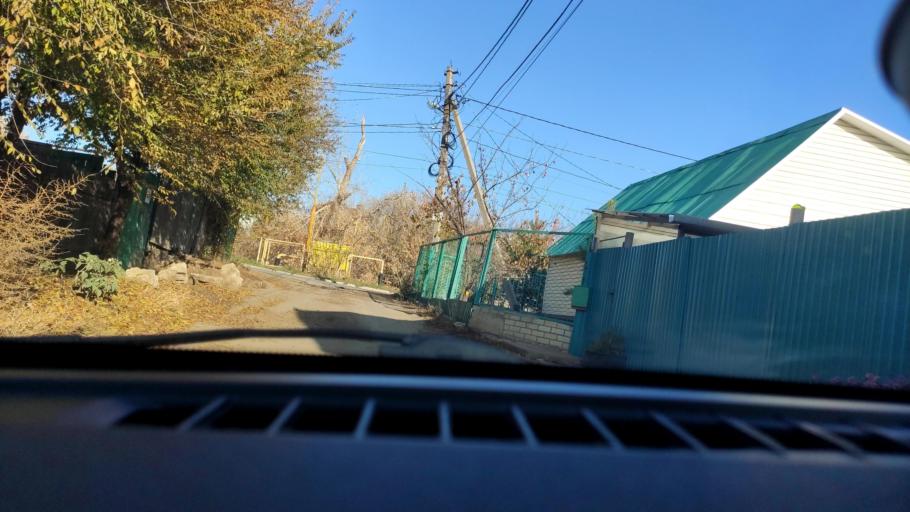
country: RU
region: Samara
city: Samara
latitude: 53.1814
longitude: 50.1552
